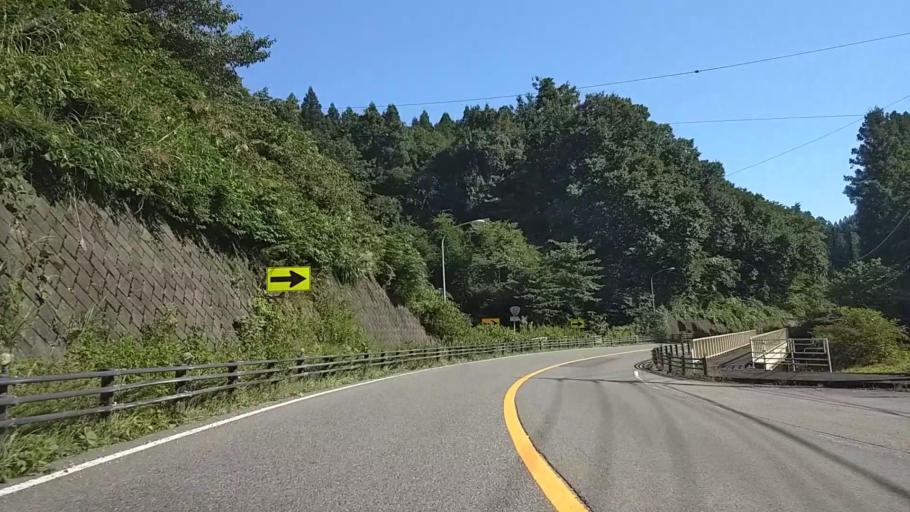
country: JP
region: Gunma
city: Annaka
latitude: 36.3355
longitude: 138.7175
